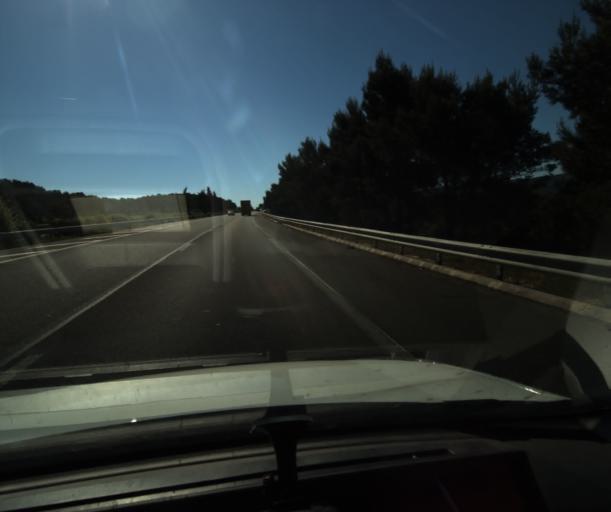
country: FR
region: Languedoc-Roussillon
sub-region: Departement de l'Aude
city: Palaja
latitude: 43.1902
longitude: 2.3798
